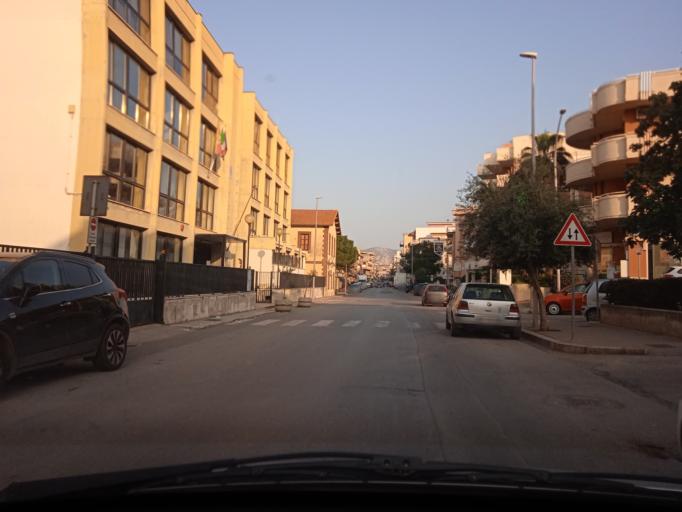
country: IT
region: Sicily
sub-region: Palermo
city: Villabate
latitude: 38.0756
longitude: 13.4428
